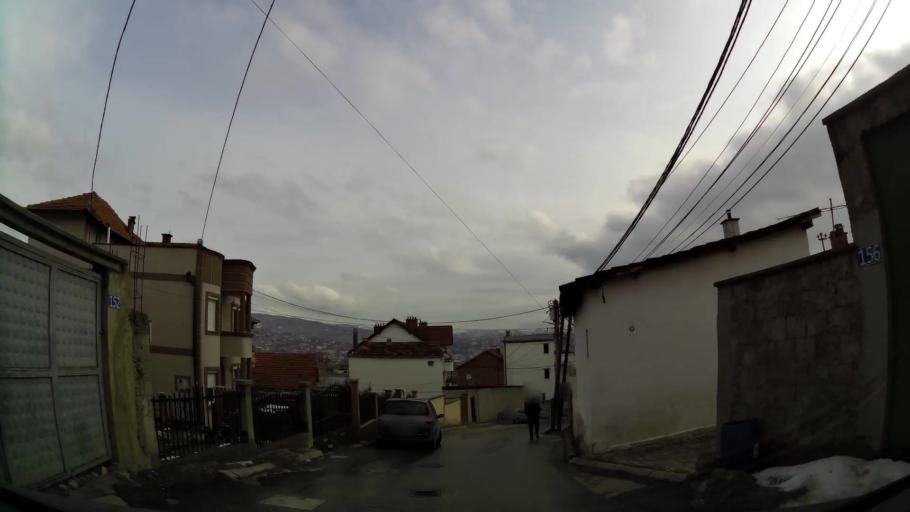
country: XK
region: Pristina
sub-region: Komuna e Prishtines
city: Pristina
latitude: 42.6743
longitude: 21.1588
